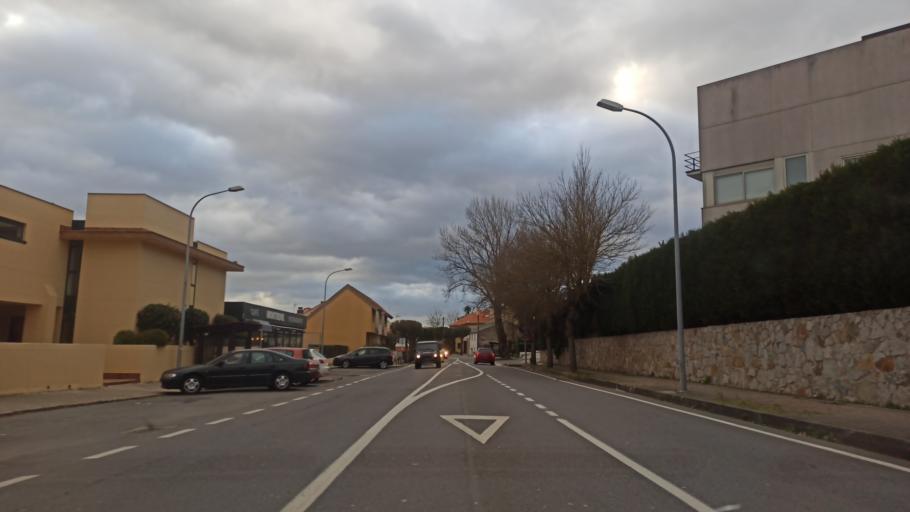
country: ES
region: Galicia
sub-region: Provincia da Coruna
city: Oleiros
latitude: 43.3293
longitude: -8.3496
